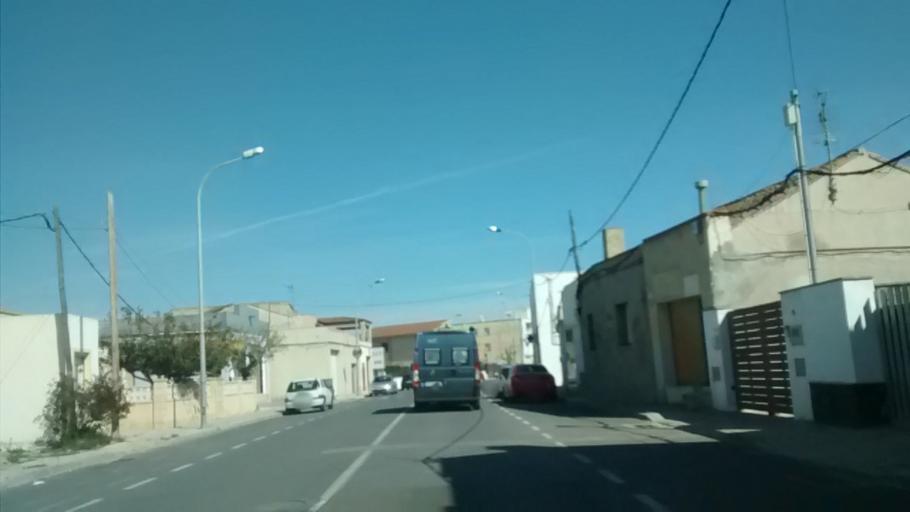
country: ES
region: Catalonia
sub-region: Provincia de Tarragona
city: Deltebre
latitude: 40.7184
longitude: 0.7290
